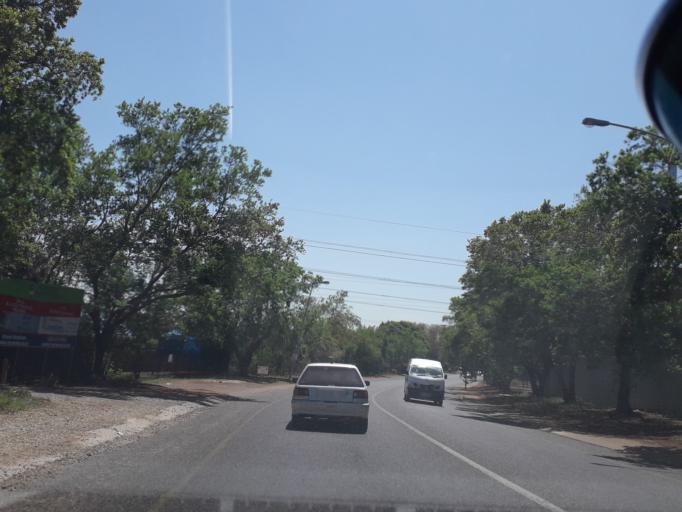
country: ZA
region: Gauteng
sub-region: City of Tshwane Metropolitan Municipality
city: Centurion
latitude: -25.8880
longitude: 28.1519
